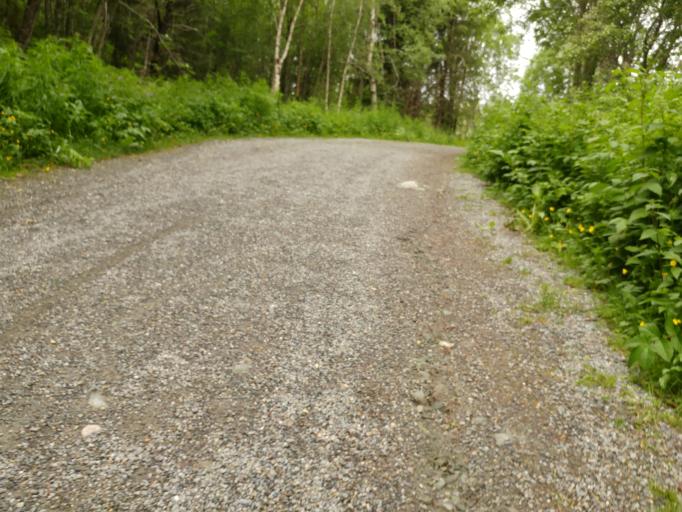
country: NO
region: Sor-Trondelag
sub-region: Melhus
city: Melhus
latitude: 63.3845
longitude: 10.2954
